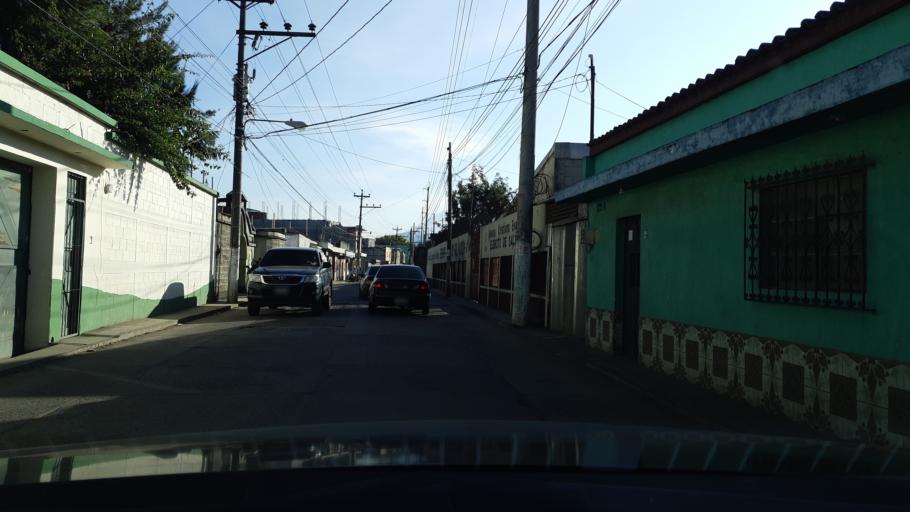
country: GT
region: Chimaltenango
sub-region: Municipio de Chimaltenango
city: Chimaltenango
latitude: 14.6577
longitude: -90.8096
